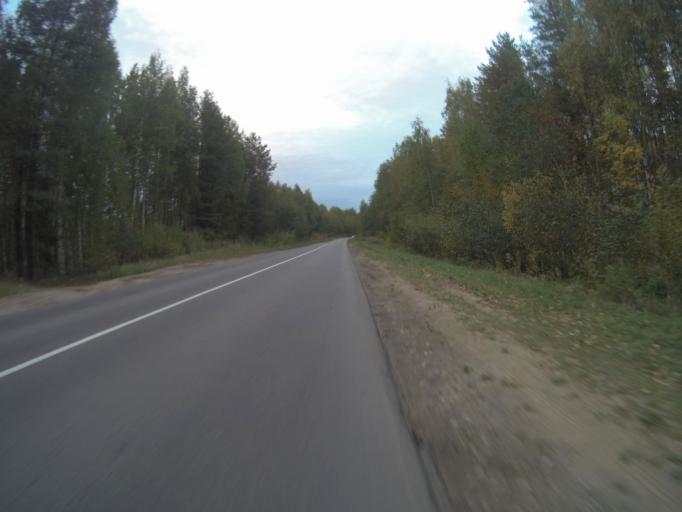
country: RU
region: Vladimir
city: Vorsha
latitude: 56.0091
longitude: 40.1112
